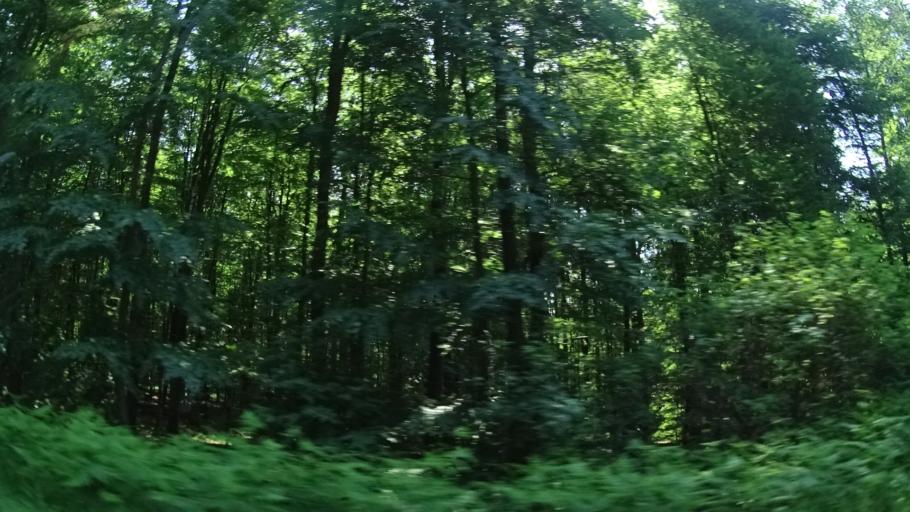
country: DE
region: Hesse
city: Rosenthal
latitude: 50.9449
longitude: 8.8486
